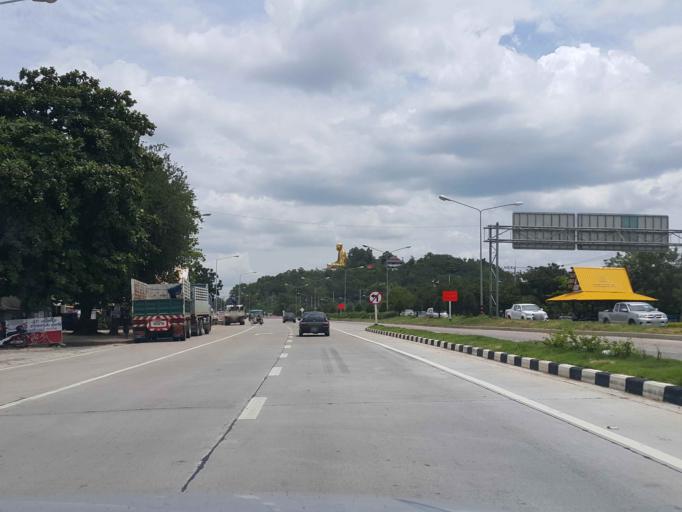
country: TH
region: Lamphun
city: Lamphun
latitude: 18.5519
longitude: 99.0494
